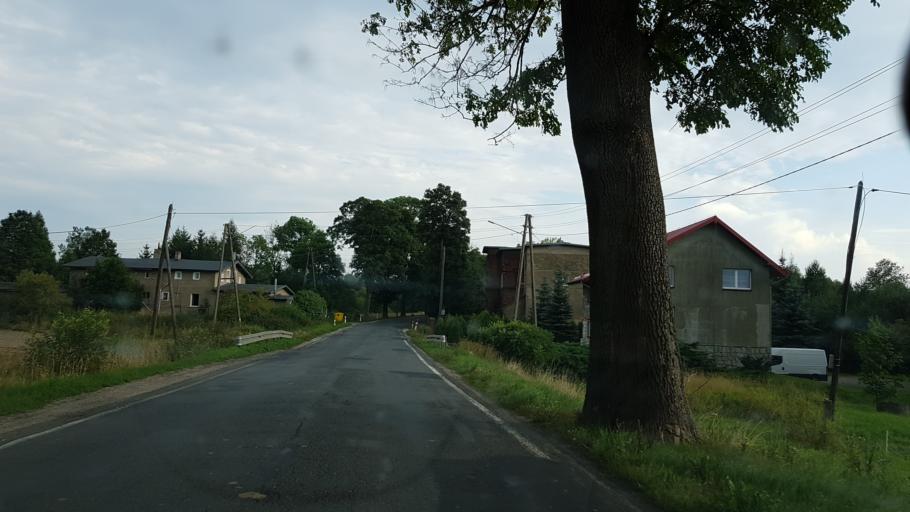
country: PL
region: Lower Silesian Voivodeship
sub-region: Powiat kamiennogorski
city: Marciszow
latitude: 50.8661
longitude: 15.9994
